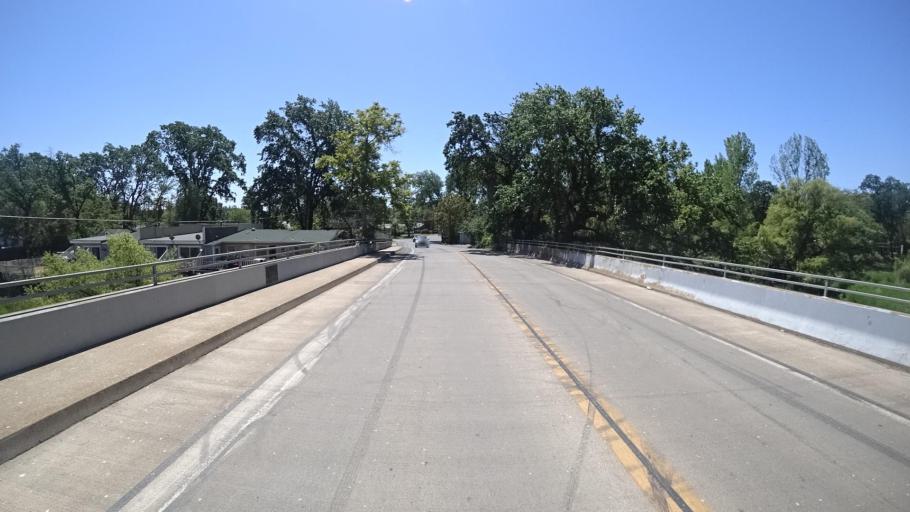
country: US
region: California
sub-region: Lake County
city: Lower Lake
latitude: 38.9258
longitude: -122.6117
